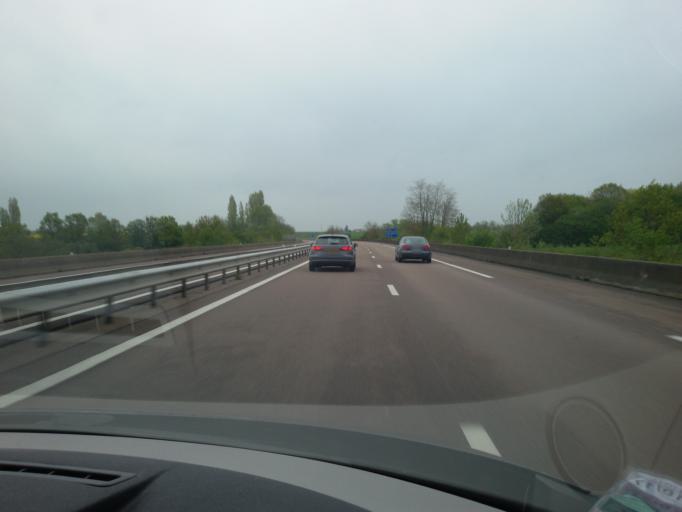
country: FR
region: Bourgogne
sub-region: Departement de la Cote-d'Or
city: Fenay
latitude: 47.2434
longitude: 5.0360
